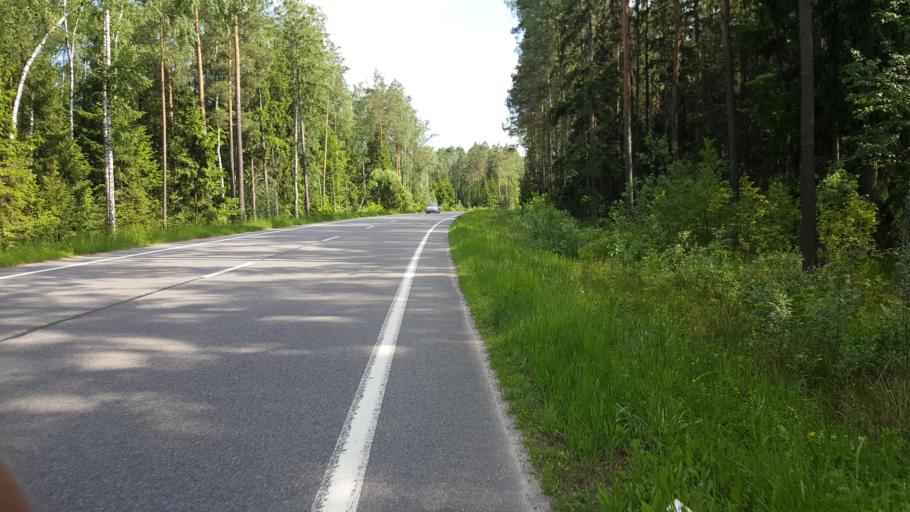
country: BY
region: Brest
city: Pruzhany
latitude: 52.5187
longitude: 24.1788
